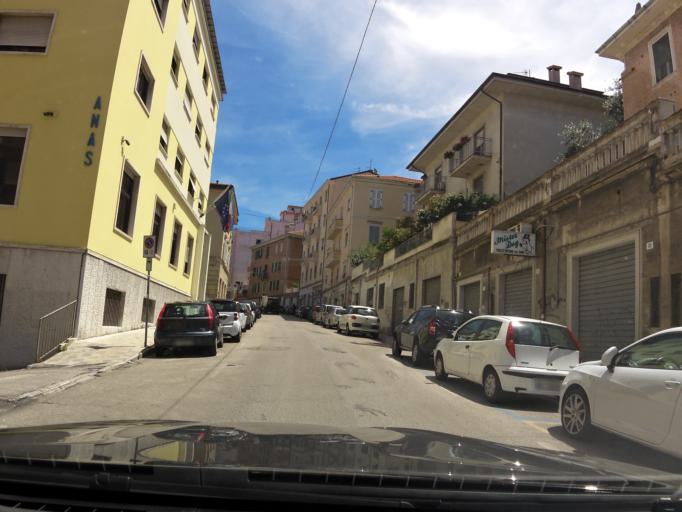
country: IT
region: The Marches
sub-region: Provincia di Ancona
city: Le Grazie di Ancona
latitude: 43.6147
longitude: 13.5192
